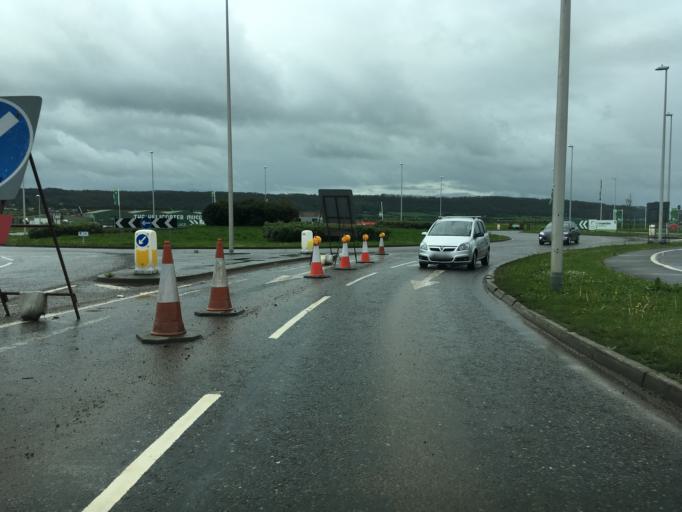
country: GB
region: England
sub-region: North Somerset
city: Hutton
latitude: 51.3423
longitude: -2.9320
